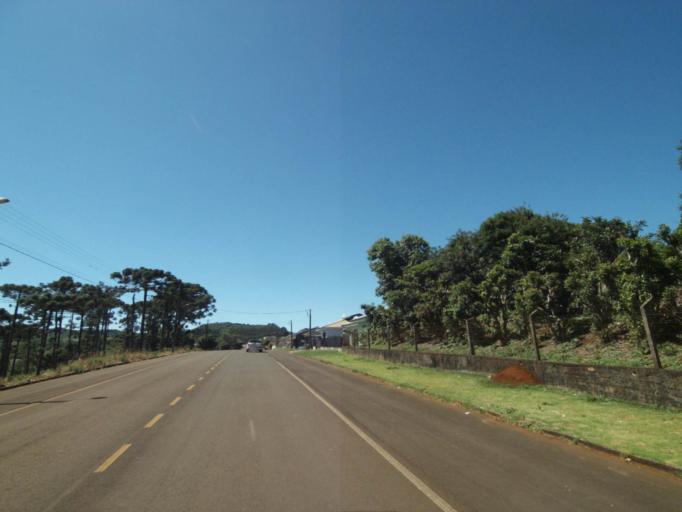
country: BR
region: Santa Catarina
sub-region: Sao Lourenco Do Oeste
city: Sao Lourenco dOeste
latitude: -26.2686
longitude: -52.7805
